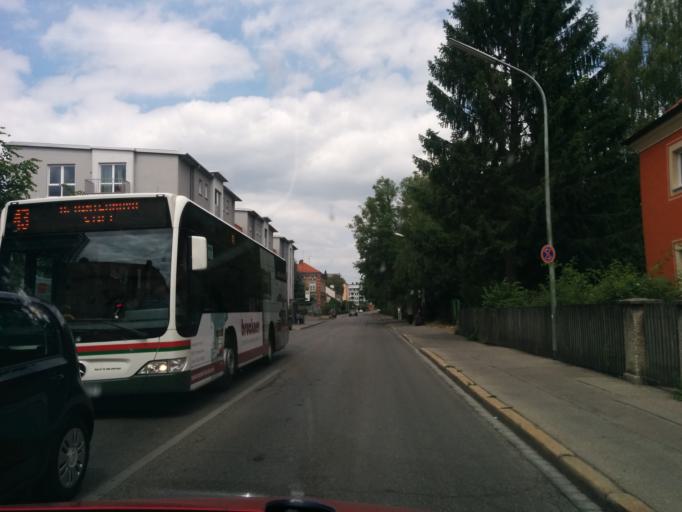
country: DE
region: Bavaria
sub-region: Swabia
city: Augsburg
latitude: 48.3529
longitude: 10.8981
